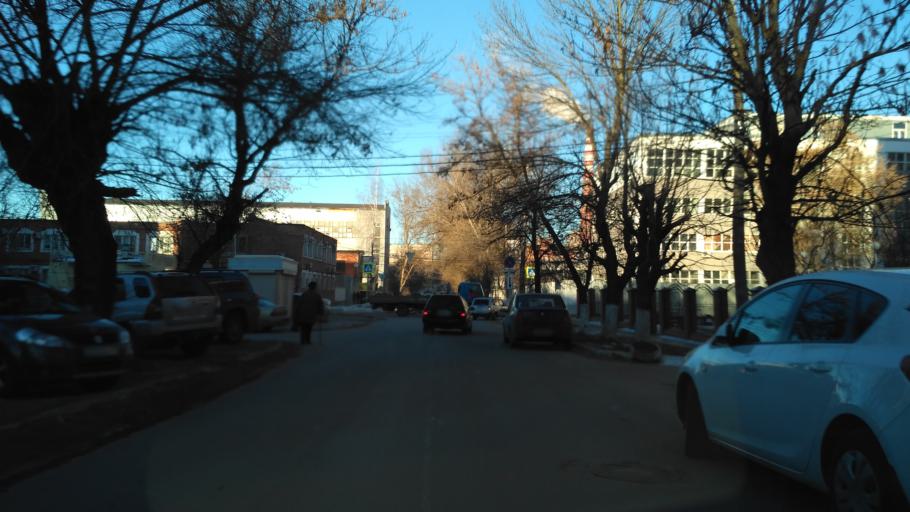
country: RU
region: Tula
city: Tula
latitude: 54.2096
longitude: 37.6094
